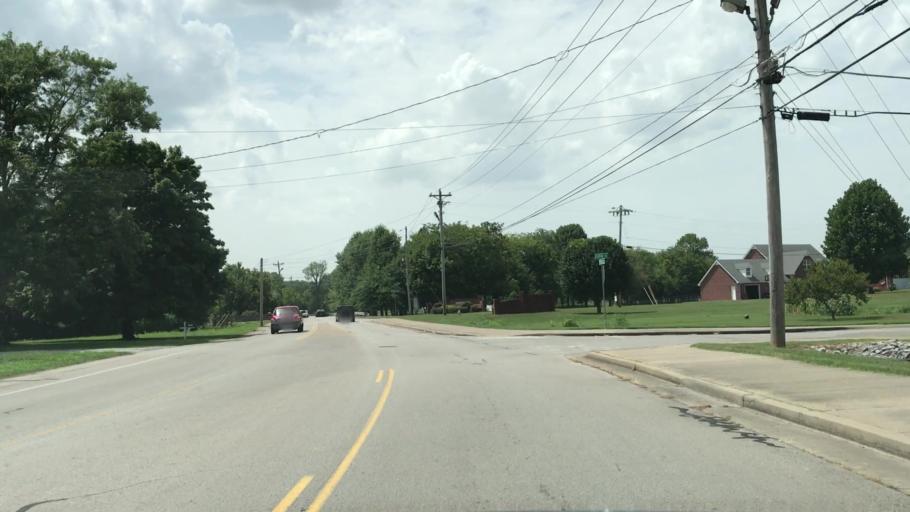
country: US
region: Tennessee
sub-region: Rutherford County
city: La Vergne
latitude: 35.9604
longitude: -86.5815
